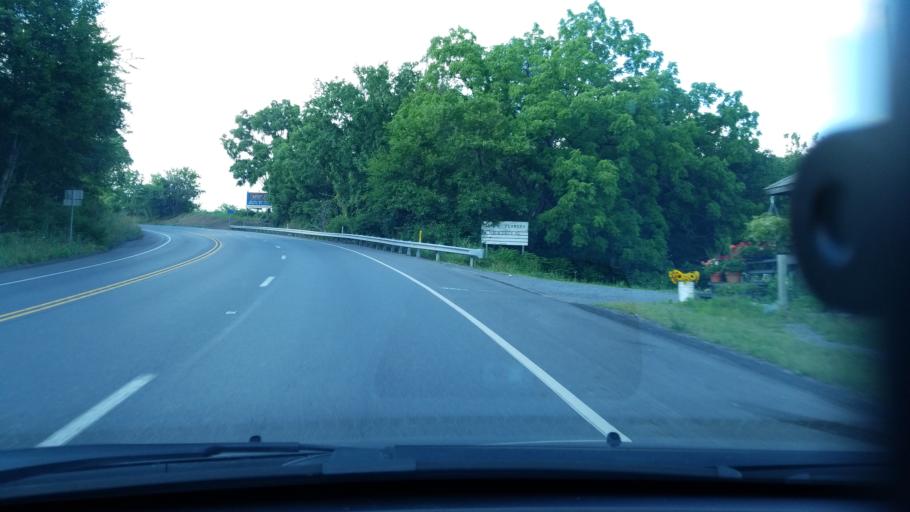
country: US
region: Pennsylvania
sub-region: Northumberland County
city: Elysburg
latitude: 40.8811
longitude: -76.5505
